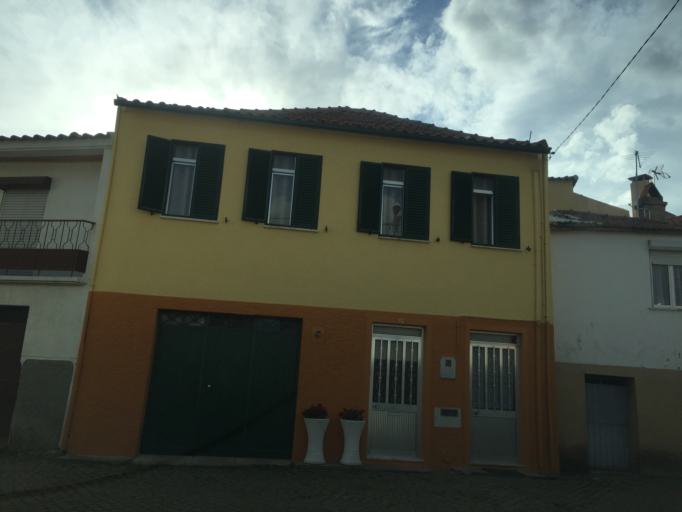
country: PT
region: Braganca
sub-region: Alfandega da Fe
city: Alfandega da Fe
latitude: 41.3416
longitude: -6.9659
